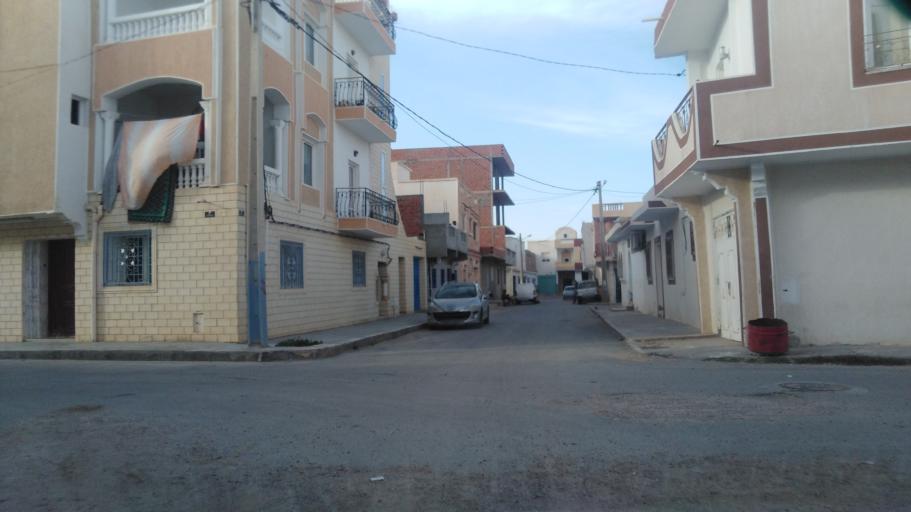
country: TN
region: Tataouine
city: Tataouine
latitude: 32.9380
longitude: 10.4540
